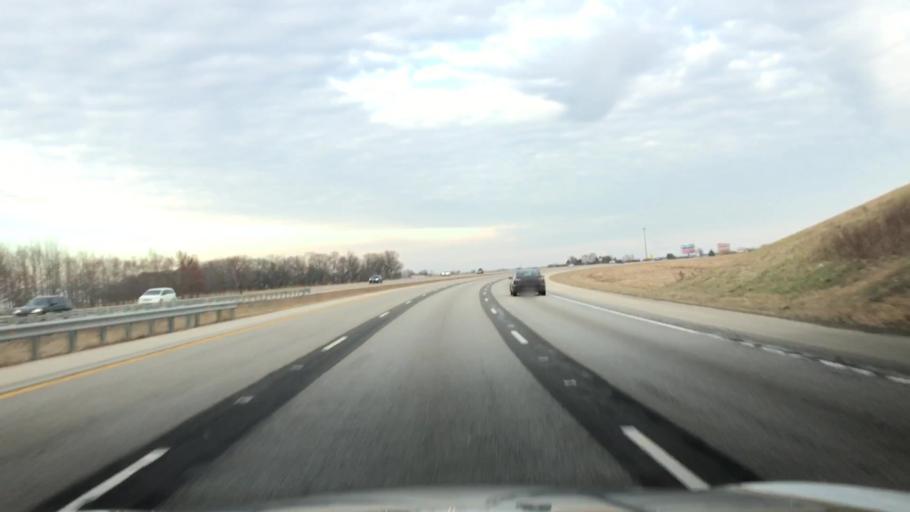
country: US
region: Illinois
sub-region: Sangamon County
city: Williamsville
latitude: 40.0204
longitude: -89.4962
